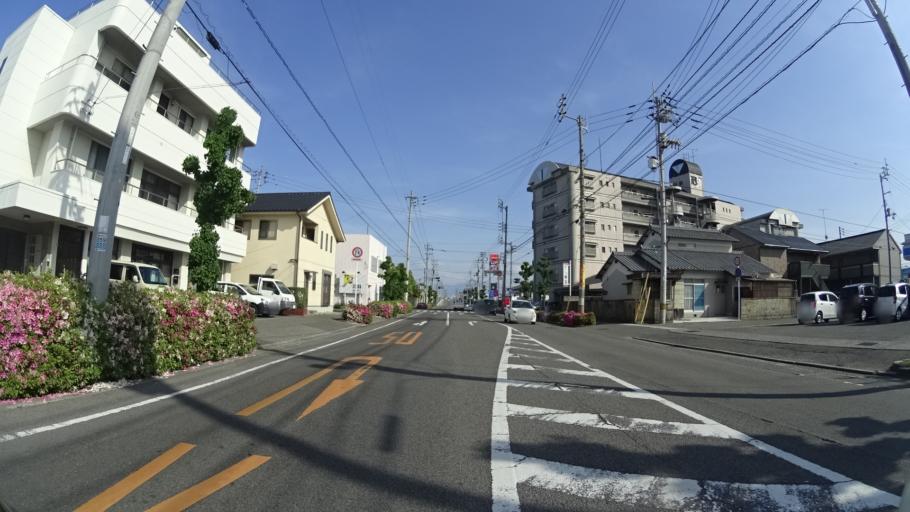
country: JP
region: Ehime
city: Saijo
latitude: 34.0613
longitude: 133.0111
